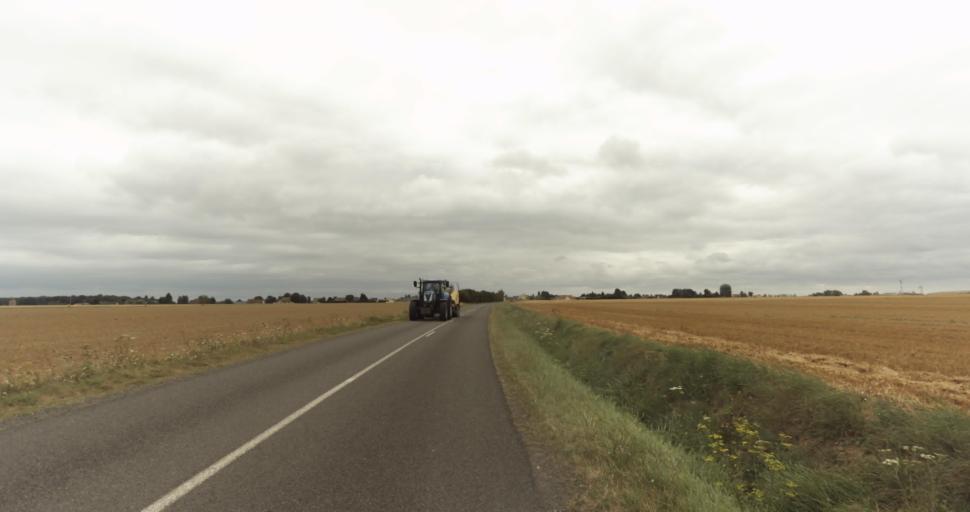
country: FR
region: Haute-Normandie
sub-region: Departement de l'Eure
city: Gravigny
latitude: 49.0389
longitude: 1.2384
